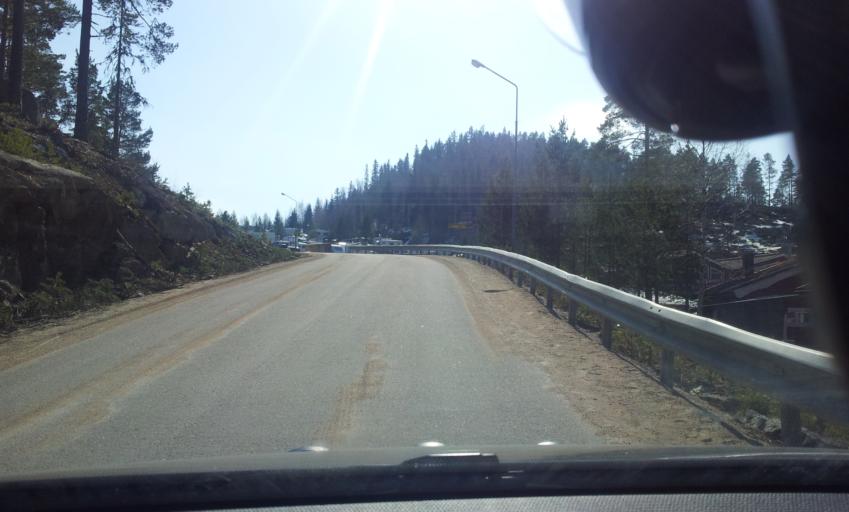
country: SE
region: Gaevleborg
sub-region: Ljusdals Kommun
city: Jaervsoe
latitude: 61.7231
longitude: 16.1591
